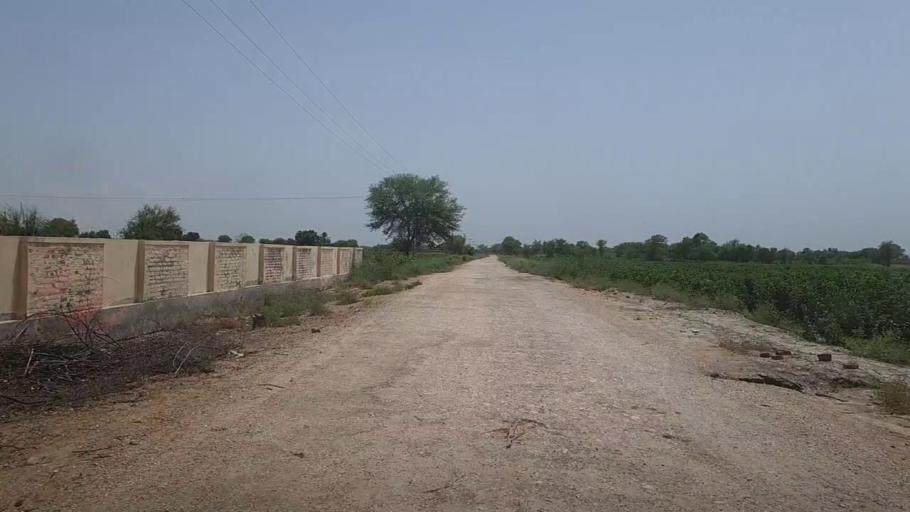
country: PK
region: Sindh
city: Pad Idan
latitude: 26.8391
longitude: 68.3248
